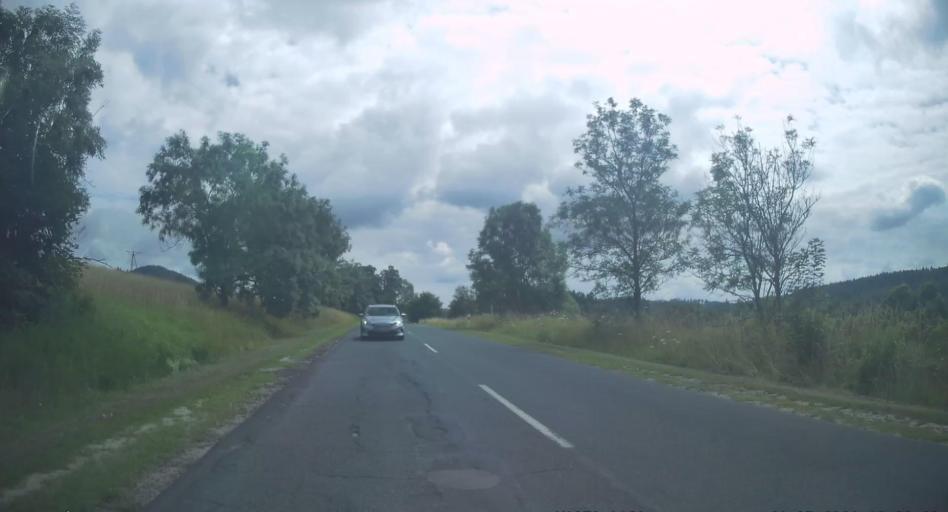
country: PL
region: Lower Silesian Voivodeship
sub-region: Powiat walbrzyski
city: Czarny Bor
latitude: 50.7727
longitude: 16.1563
